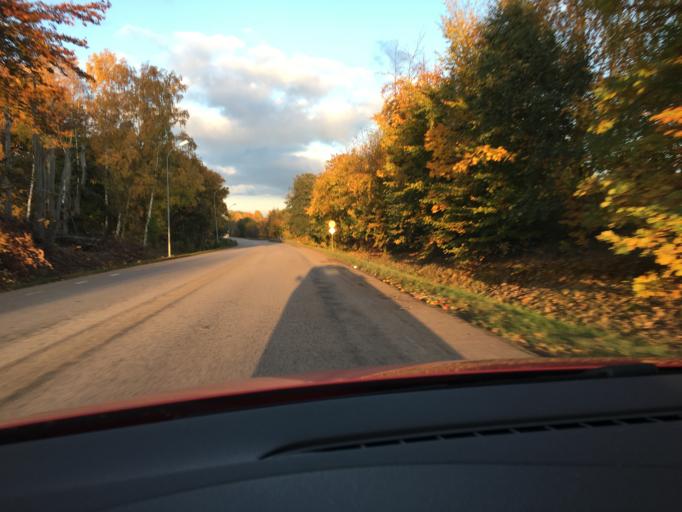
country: SE
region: Skane
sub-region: Bjuvs Kommun
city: Bjuv
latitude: 56.0796
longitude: 12.9163
